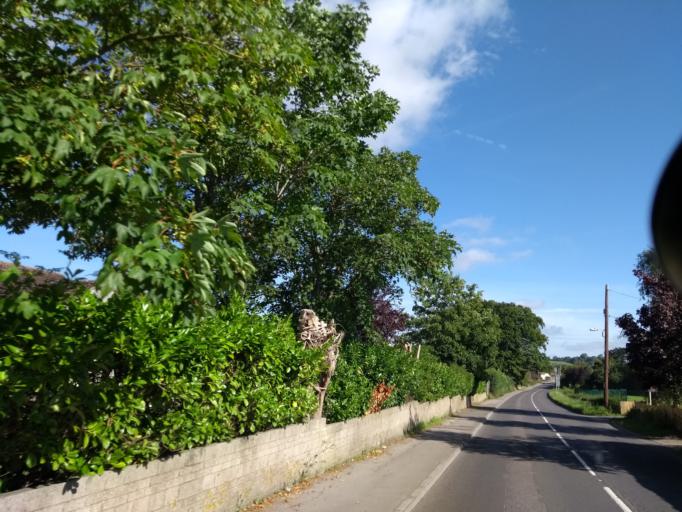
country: GB
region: England
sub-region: Somerset
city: Langport
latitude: 51.0389
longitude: -2.8190
